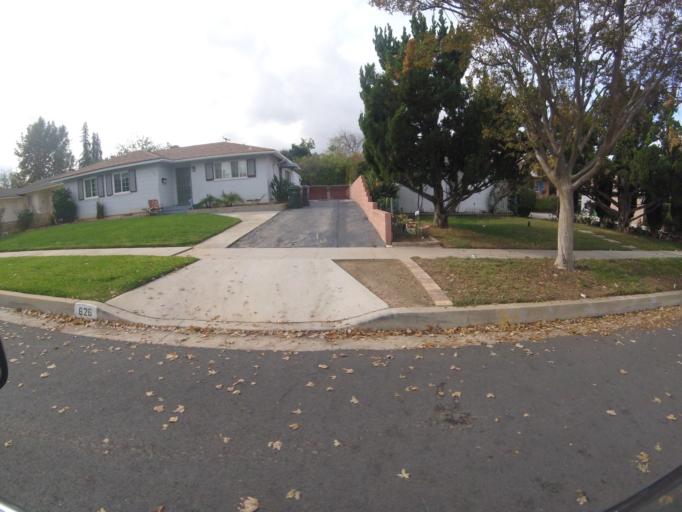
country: US
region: California
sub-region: San Bernardino County
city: Redlands
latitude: 34.0431
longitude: -117.1816
